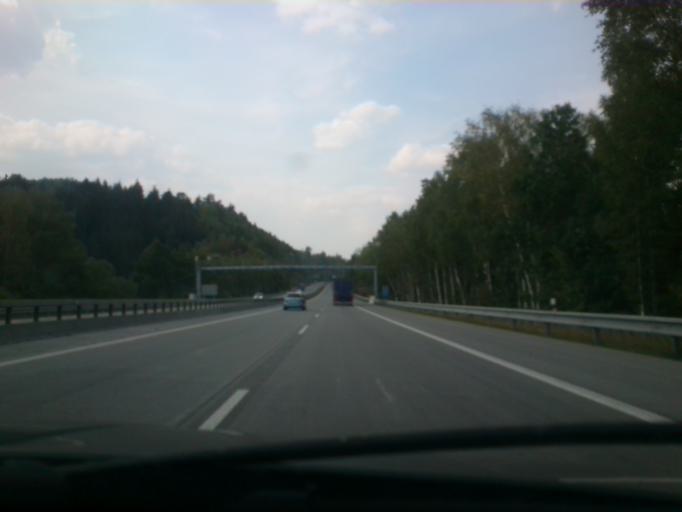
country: CZ
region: Central Bohemia
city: Divisov
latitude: 49.7826
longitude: 14.9313
